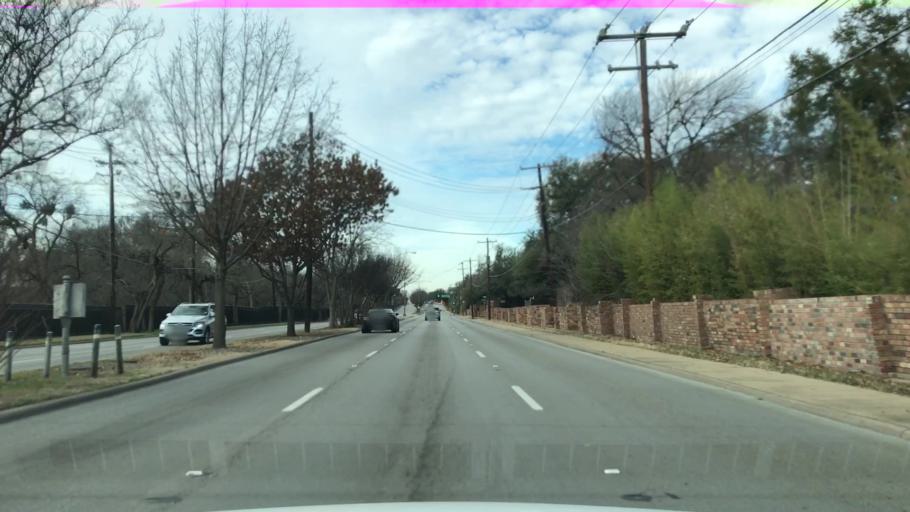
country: US
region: Texas
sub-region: Dallas County
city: University Park
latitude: 32.8801
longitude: -96.7761
